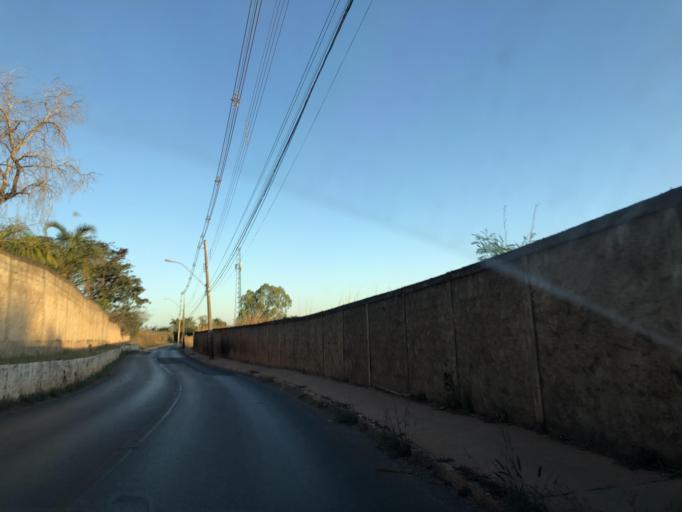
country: BR
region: Federal District
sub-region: Brasilia
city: Brasilia
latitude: -15.8708
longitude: -47.7828
